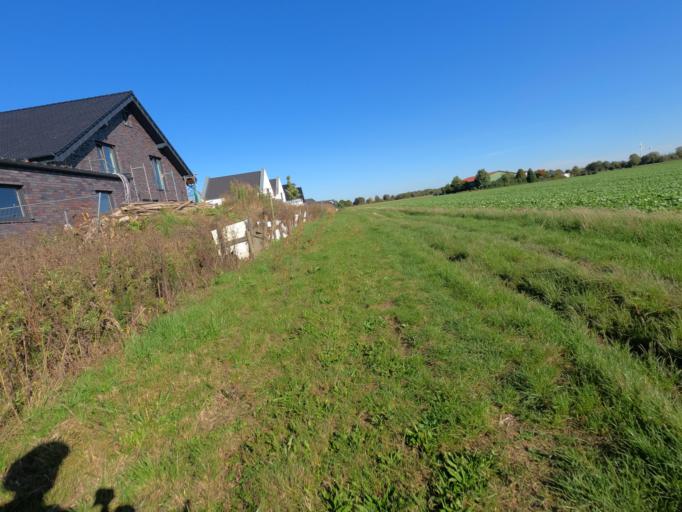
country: DE
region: North Rhine-Westphalia
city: Erkelenz
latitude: 51.0568
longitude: 6.3473
